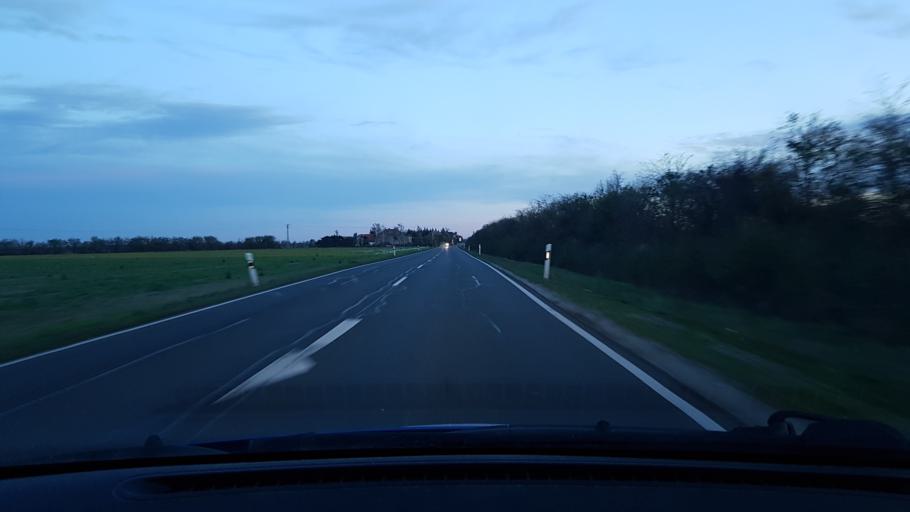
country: DE
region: Saxony-Anhalt
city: Zerbst
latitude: 52.0075
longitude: 12.0241
